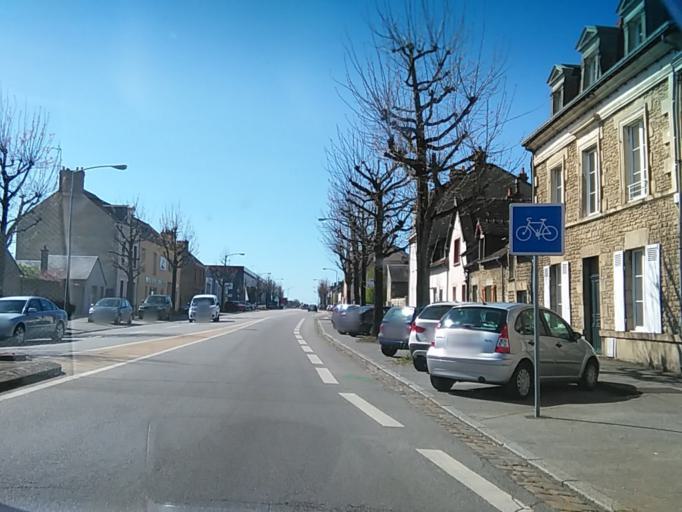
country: FR
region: Lower Normandy
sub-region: Departement de l'Orne
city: Alencon
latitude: 48.4321
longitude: 0.0737
